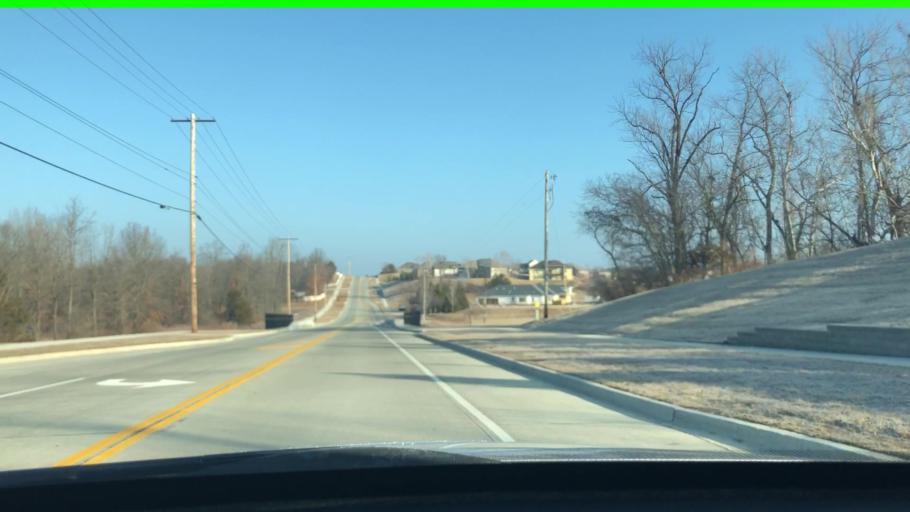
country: US
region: Missouri
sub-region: Boone County
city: Columbia
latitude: 38.9036
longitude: -92.4005
